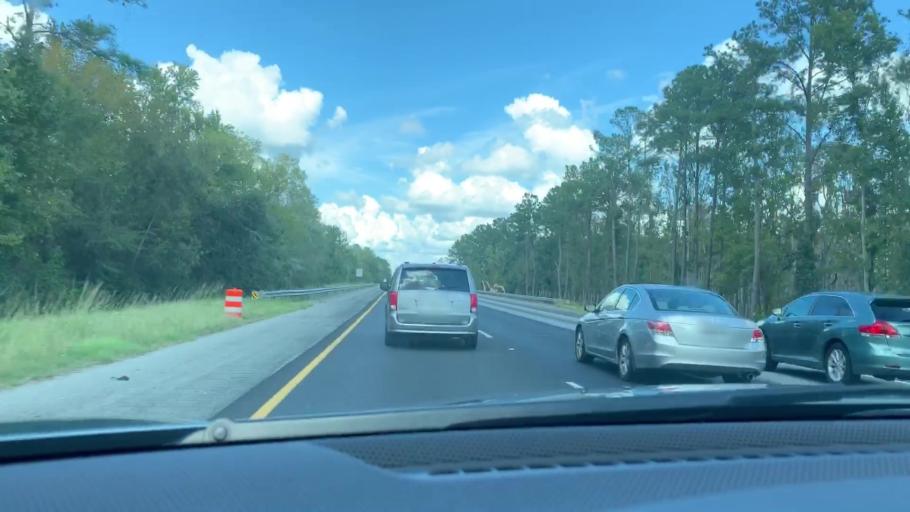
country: US
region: Georgia
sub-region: Camden County
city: Woodbine
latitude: 30.9105
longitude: -81.6859
